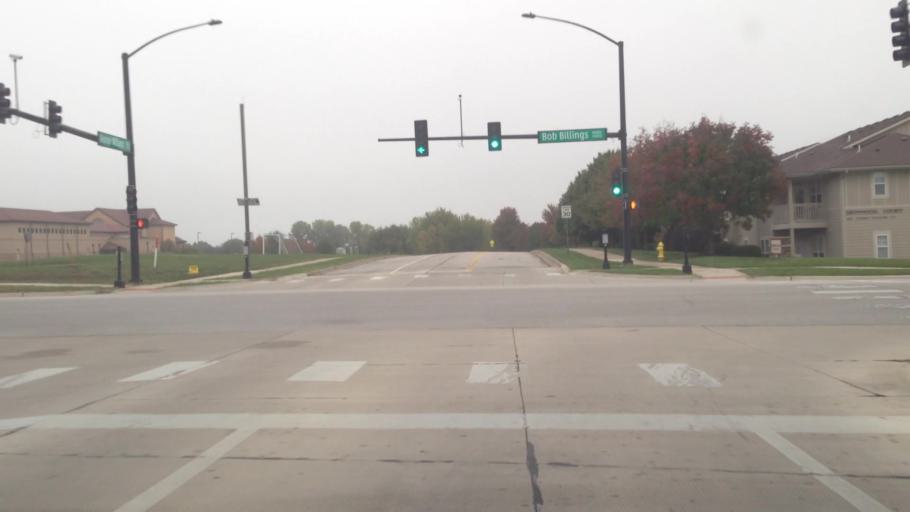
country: US
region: Kansas
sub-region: Douglas County
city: Lawrence
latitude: 38.9599
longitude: -95.3256
